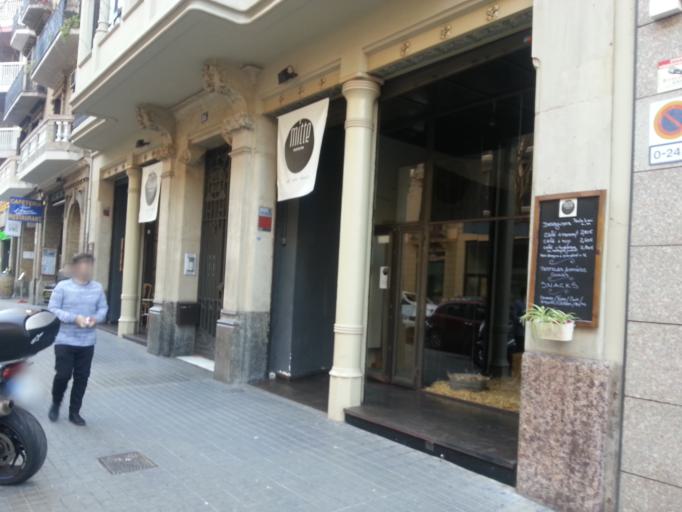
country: ES
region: Catalonia
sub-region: Provincia de Barcelona
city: Eixample
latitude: 41.3961
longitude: 2.1716
